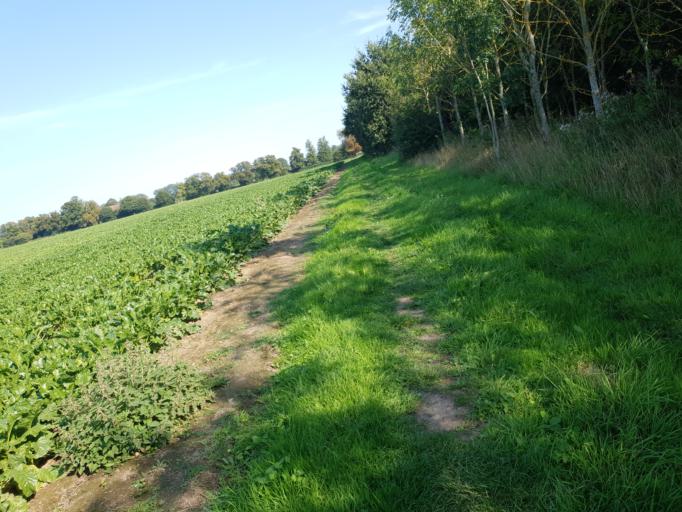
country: GB
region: England
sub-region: Suffolk
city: East Bergholt
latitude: 51.9499
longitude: 1.0082
